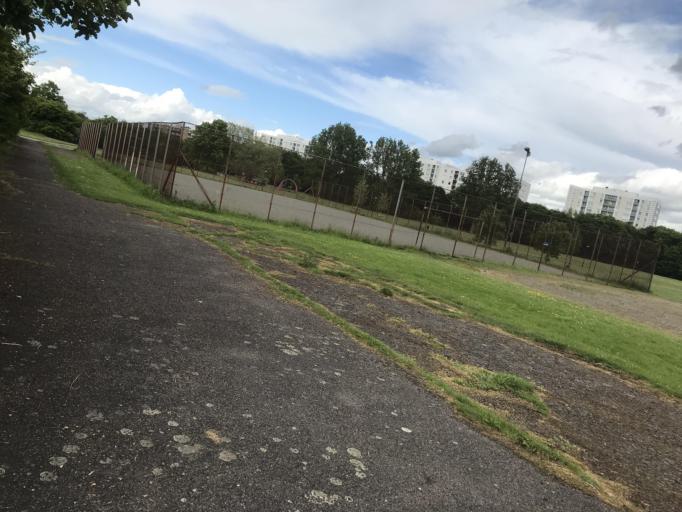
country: SE
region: Skane
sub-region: Burlovs Kommun
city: Arloev
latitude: 55.5770
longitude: 13.0539
